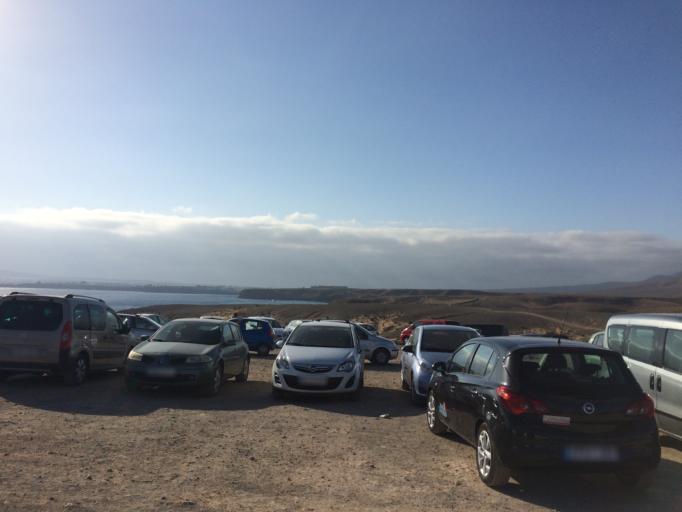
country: ES
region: Canary Islands
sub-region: Provincia de Las Palmas
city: Playa Blanca
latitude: 28.8436
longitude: -13.7865
